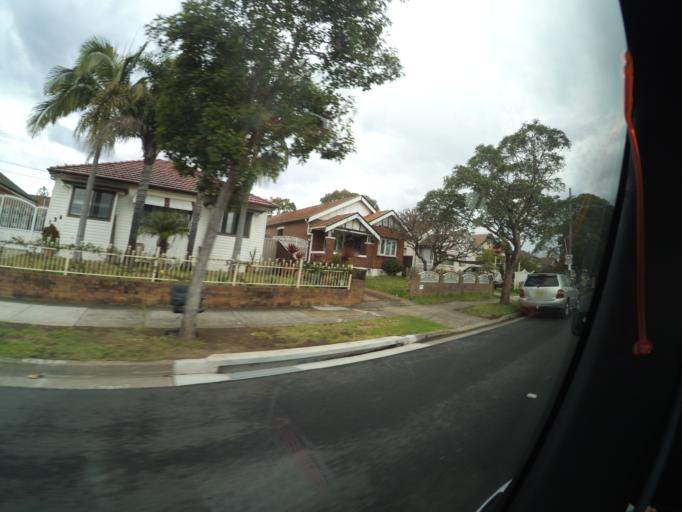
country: AU
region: New South Wales
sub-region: Bankstown
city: Bankstown
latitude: -33.9176
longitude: 151.0243
